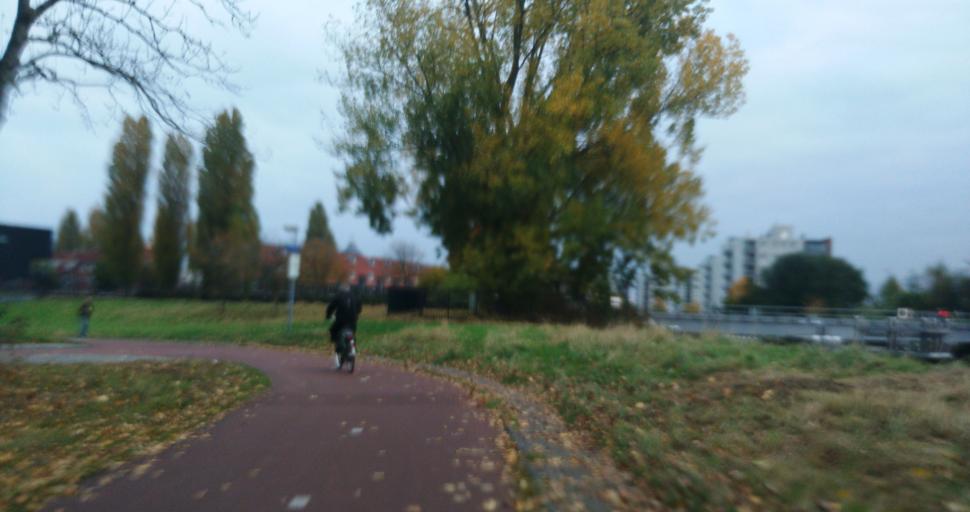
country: NL
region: Groningen
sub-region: Gemeente Groningen
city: Groningen
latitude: 53.2215
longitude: 6.5418
